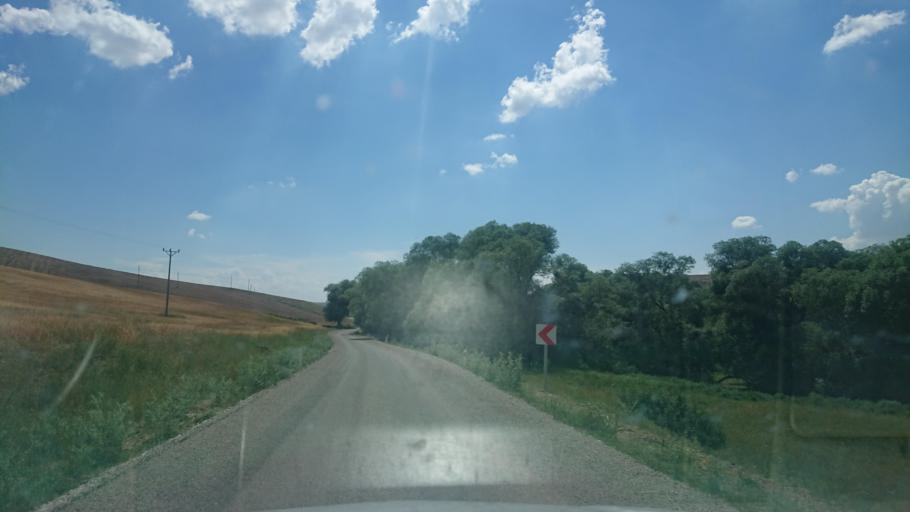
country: TR
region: Aksaray
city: Agacoren
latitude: 38.8361
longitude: 33.8043
